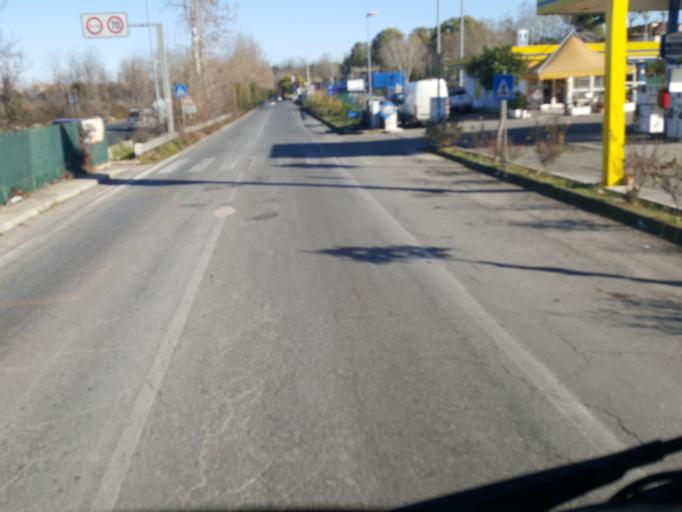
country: IT
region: Latium
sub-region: Citta metropolitana di Roma Capitale
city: Vitinia
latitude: 41.7958
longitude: 12.4047
